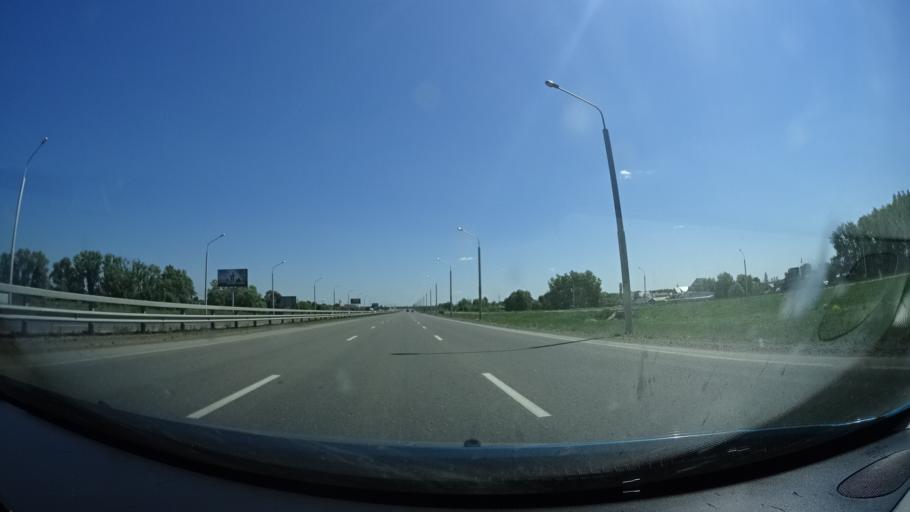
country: RU
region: Bashkortostan
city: Mikhaylovka
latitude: 54.7979
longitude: 55.8771
